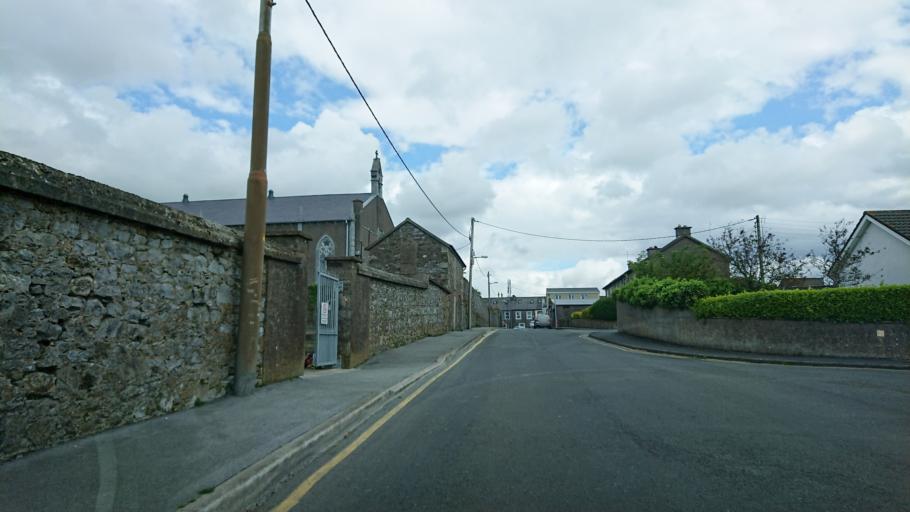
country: IE
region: Munster
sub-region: Waterford
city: Dungarvan
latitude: 52.0865
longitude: -7.6210
